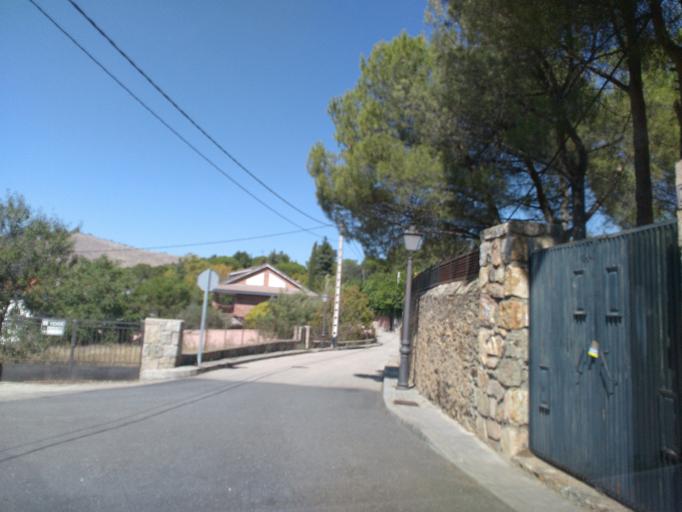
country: ES
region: Madrid
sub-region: Provincia de Madrid
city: Robledo de Chavela
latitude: 40.5206
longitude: -4.2488
